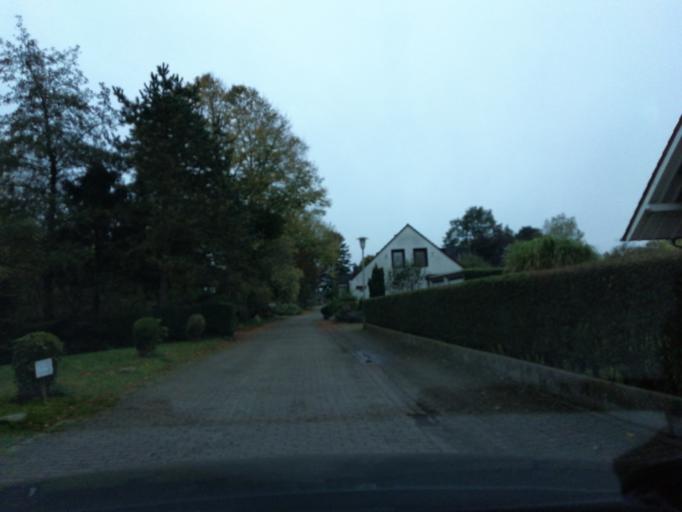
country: DE
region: Lower Saxony
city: Sillenstede
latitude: 53.6261
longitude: 8.0269
